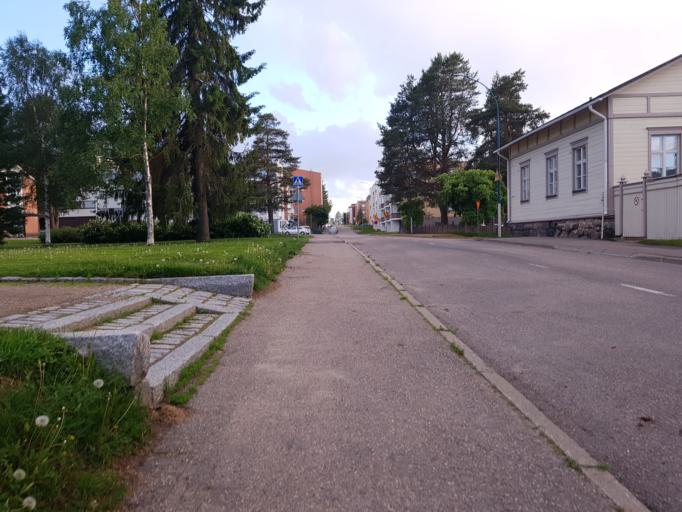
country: FI
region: Kainuu
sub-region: Kajaani
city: Kajaani
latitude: 64.2249
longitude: 27.7269
